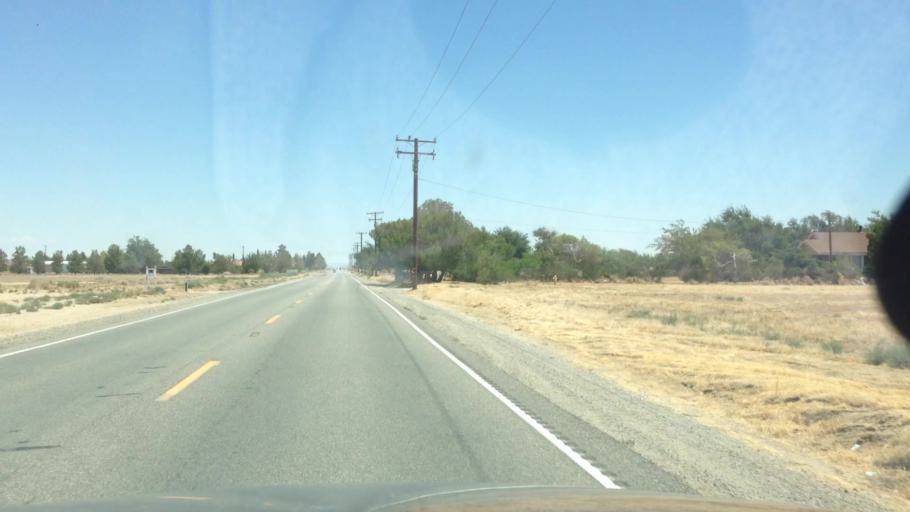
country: US
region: California
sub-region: Los Angeles County
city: Quartz Hill
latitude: 34.7764
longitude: -118.2867
